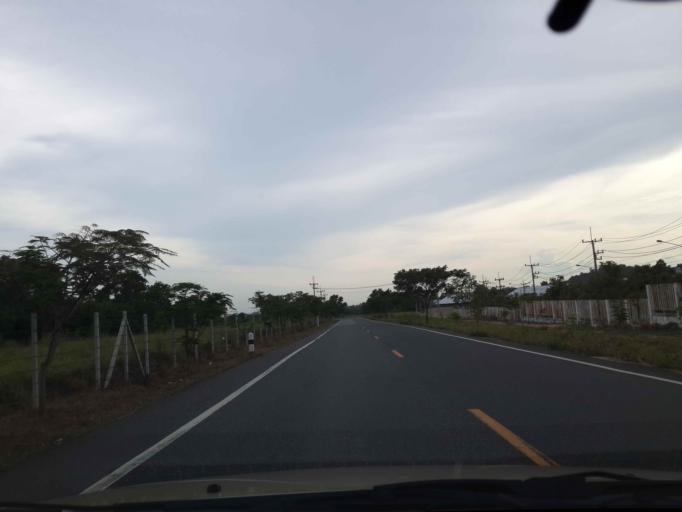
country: TH
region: Chon Buri
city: Phatthaya
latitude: 12.9168
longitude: 101.0000
